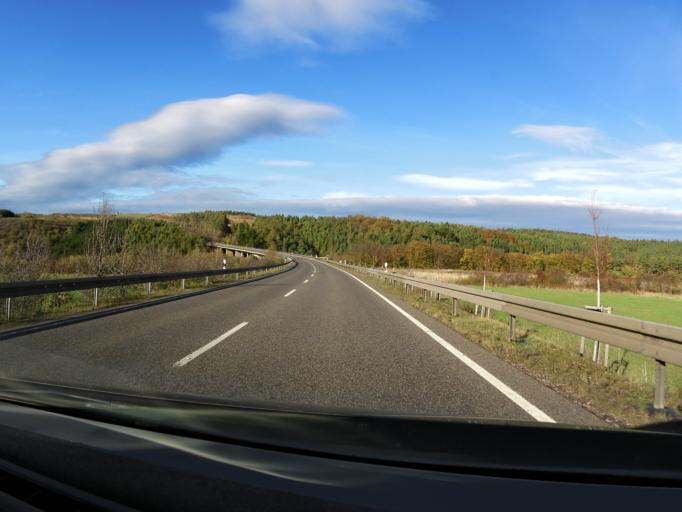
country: DE
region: Thuringia
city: Geschwenda
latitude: 50.7342
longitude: 10.8364
